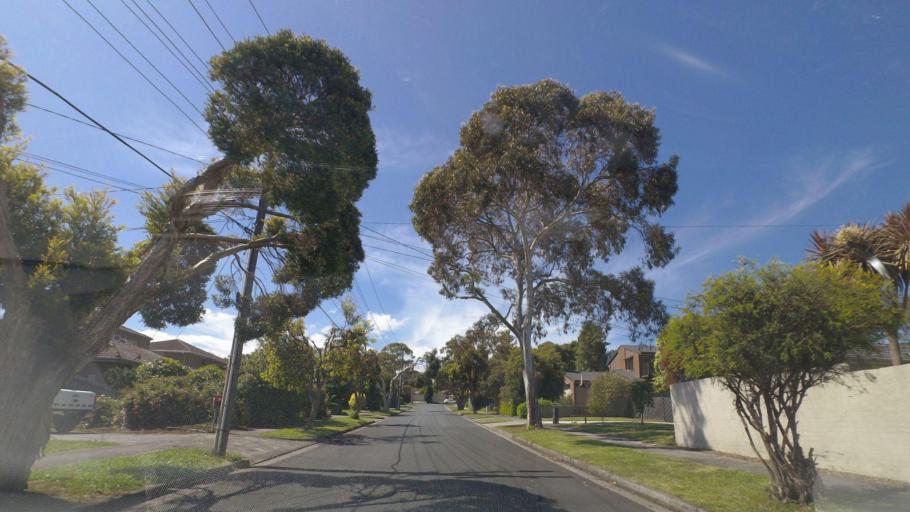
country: AU
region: Victoria
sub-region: Whitehorse
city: Vermont
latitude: -37.8516
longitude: 145.1979
